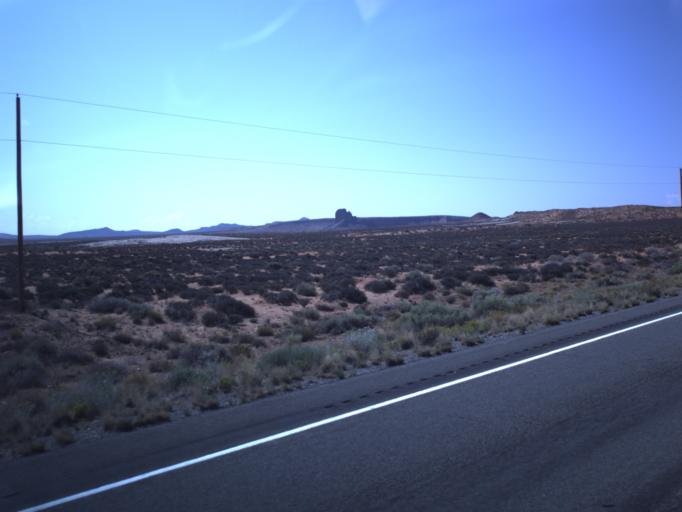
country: US
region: Utah
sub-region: San Juan County
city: Blanding
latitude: 37.0686
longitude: -109.5539
